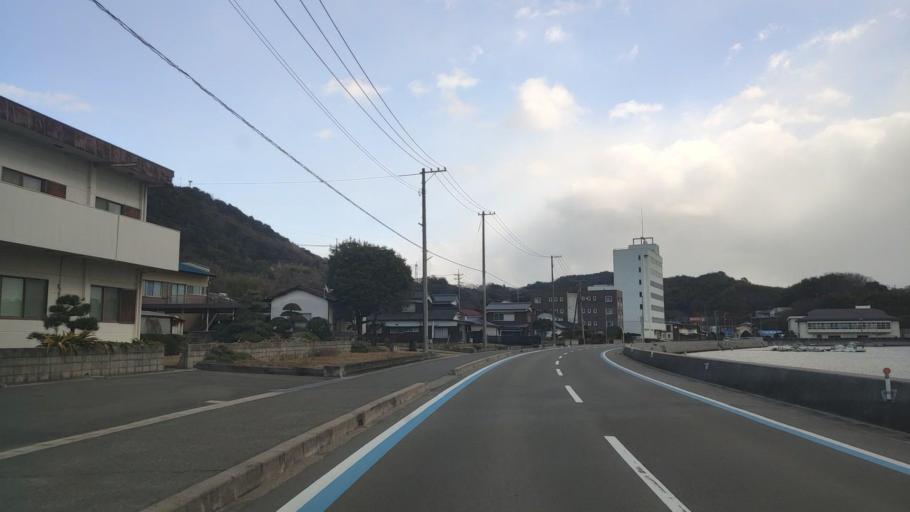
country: JP
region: Hiroshima
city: Innoshima
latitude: 34.2046
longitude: 133.0980
